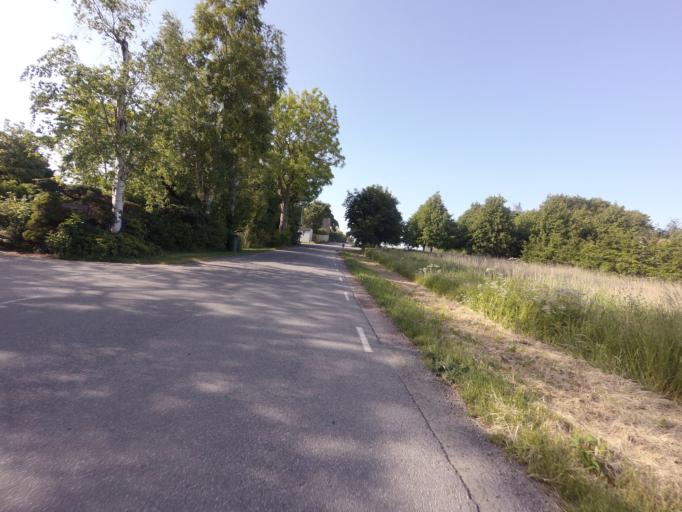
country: SE
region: Skane
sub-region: Trelleborgs Kommun
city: Skare
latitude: 55.4219
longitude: 13.0194
